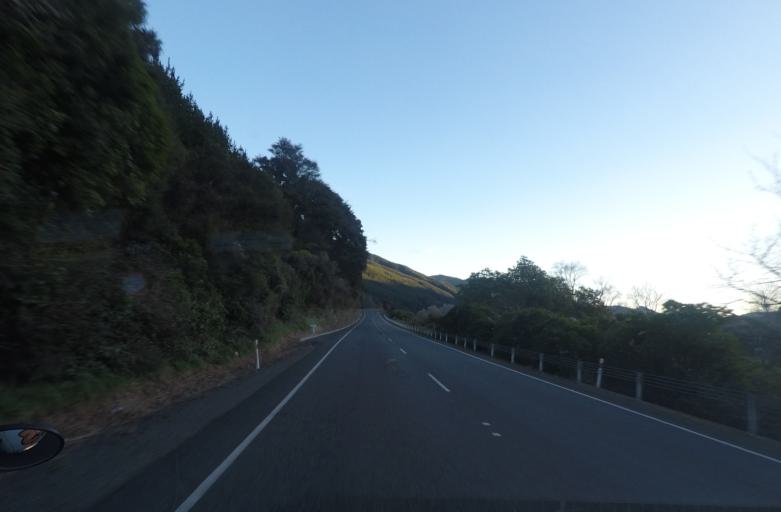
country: NZ
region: Marlborough
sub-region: Marlborough District
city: Picton
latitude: -41.2762
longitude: 173.7308
